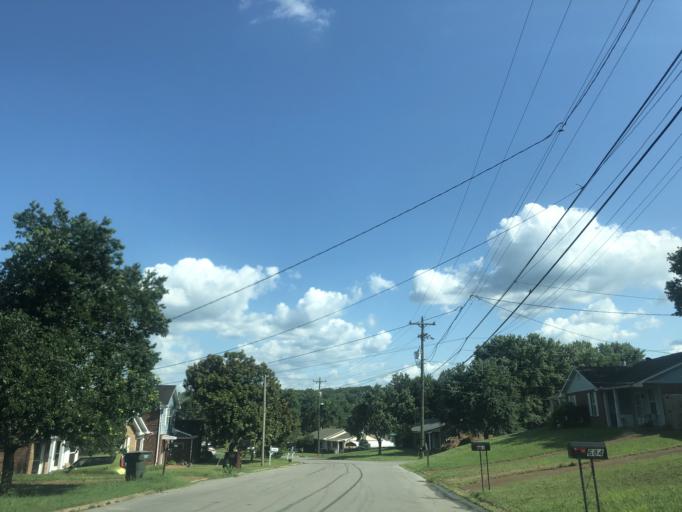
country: US
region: Tennessee
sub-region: Davidson County
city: Lakewood
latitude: 36.1995
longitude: -86.6012
